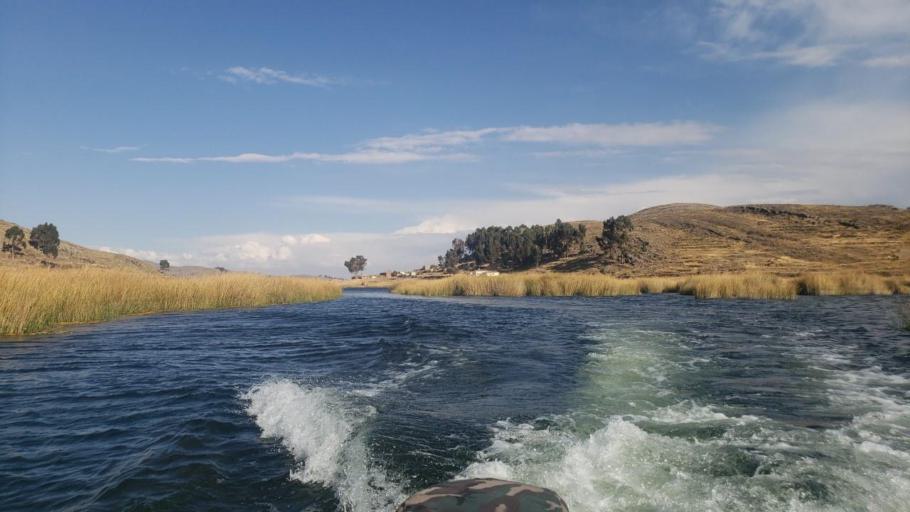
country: BO
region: La Paz
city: Huatajata
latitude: -16.3290
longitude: -68.7198
